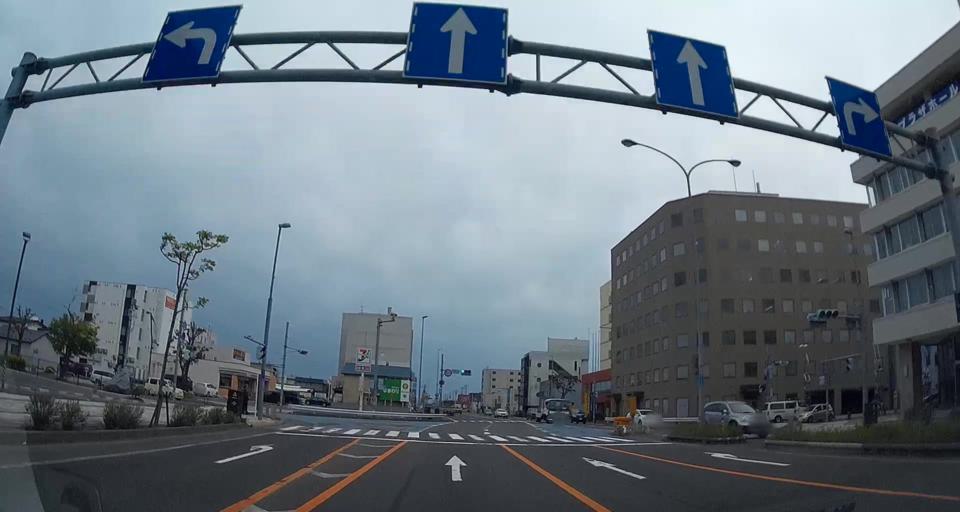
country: JP
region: Hokkaido
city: Tomakomai
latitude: 42.6327
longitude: 141.6011
